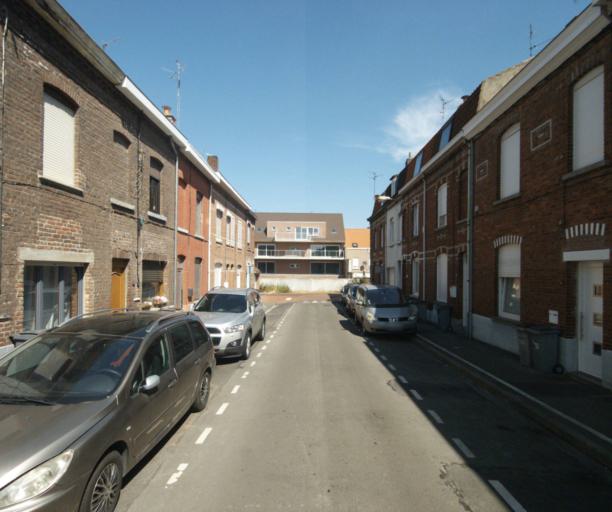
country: FR
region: Nord-Pas-de-Calais
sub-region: Departement du Nord
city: Halluin
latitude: 50.7866
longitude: 3.1319
